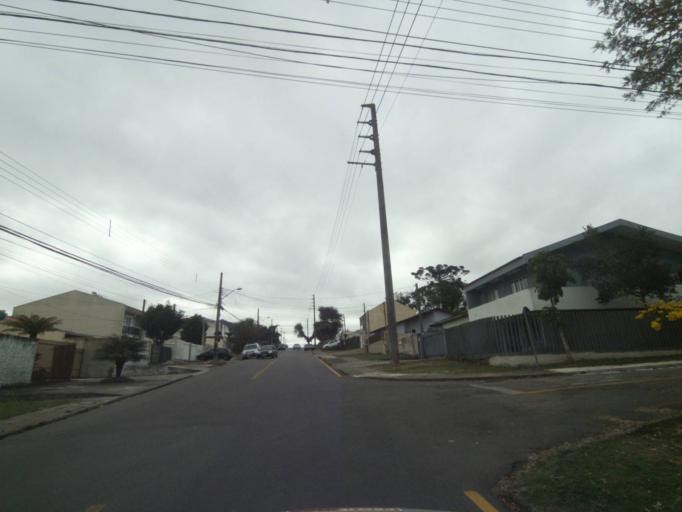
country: BR
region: Parana
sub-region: Pinhais
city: Pinhais
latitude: -25.4820
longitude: -49.2273
